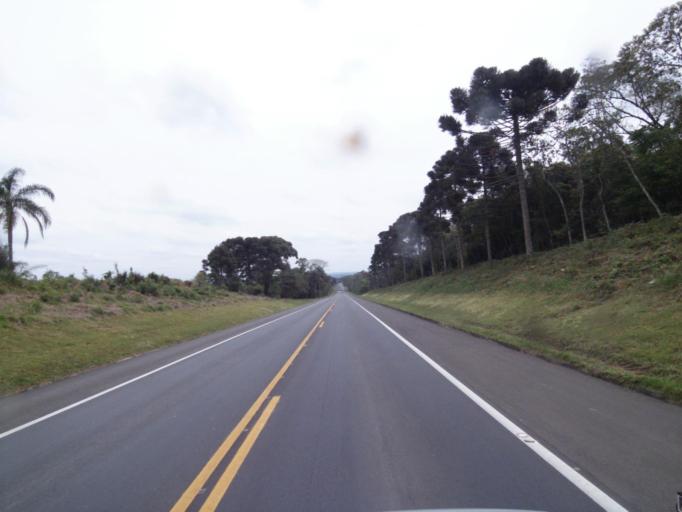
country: BR
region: Parana
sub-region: Irati
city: Irati
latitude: -25.4705
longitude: -50.4993
